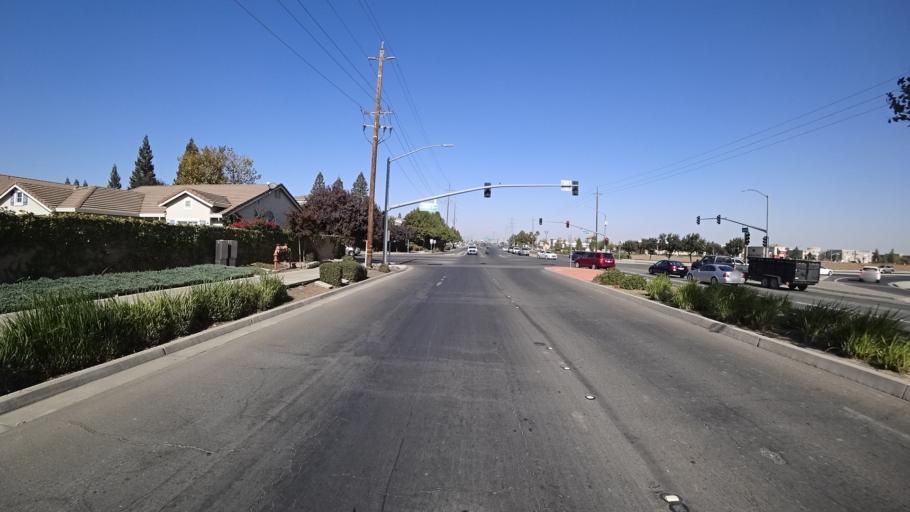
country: US
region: California
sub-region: Yolo County
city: Woodland
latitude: 38.6683
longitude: -121.7287
